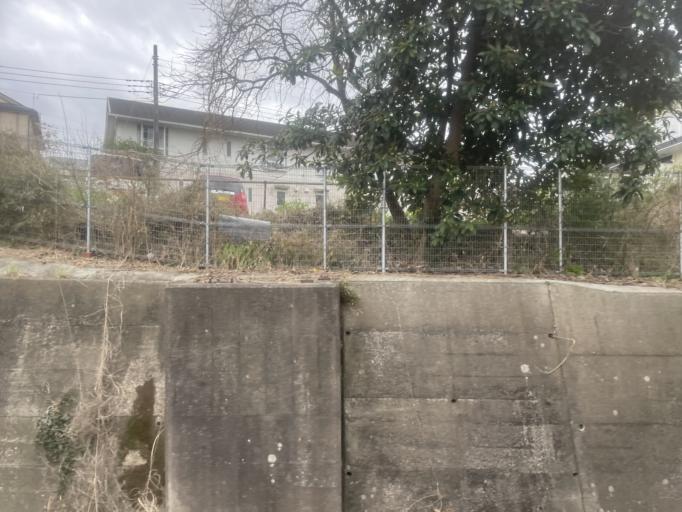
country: JP
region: Chiba
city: Oami
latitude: 35.5301
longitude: 140.2722
